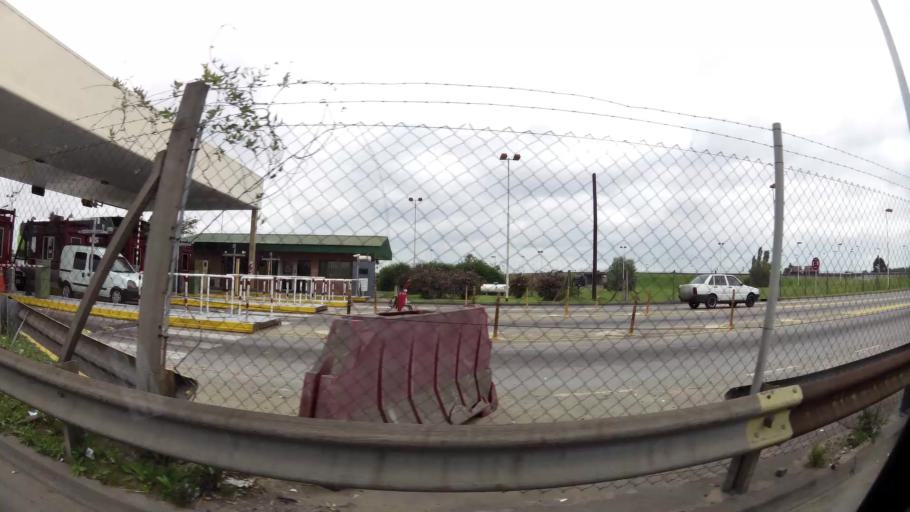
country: AR
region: Buenos Aires
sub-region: Partido de Ezeiza
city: Ezeiza
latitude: -34.8296
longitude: -58.5101
